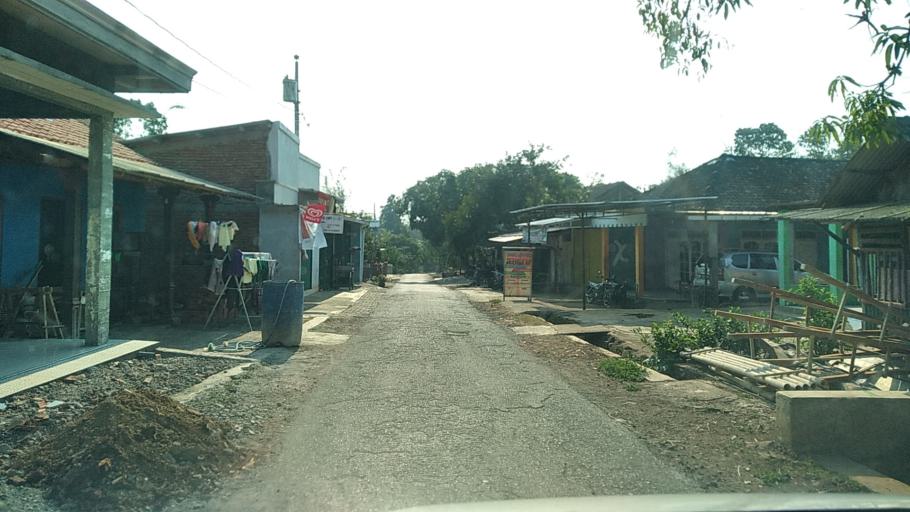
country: ID
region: Central Java
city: Semarang
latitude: -7.0263
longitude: 110.3106
